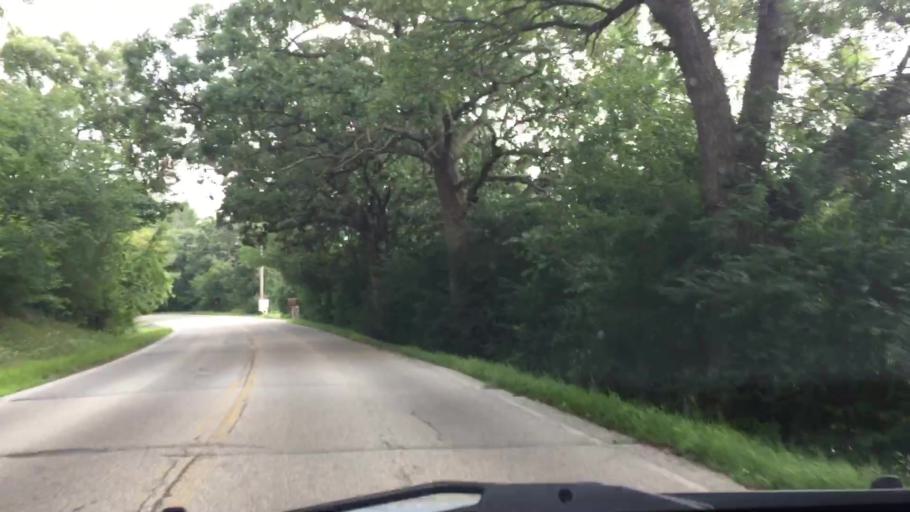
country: US
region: Wisconsin
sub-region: Waukesha County
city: Wales
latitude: 43.0291
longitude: -88.3654
